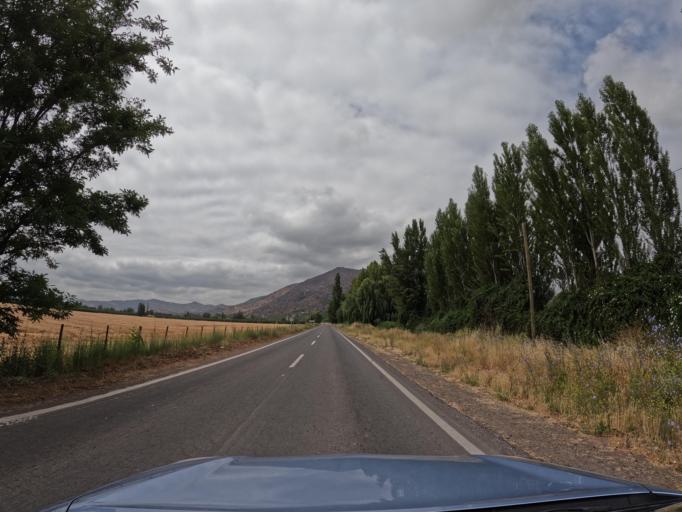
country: CL
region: Maule
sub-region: Provincia de Curico
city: Teno
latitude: -34.7531
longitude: -71.2177
